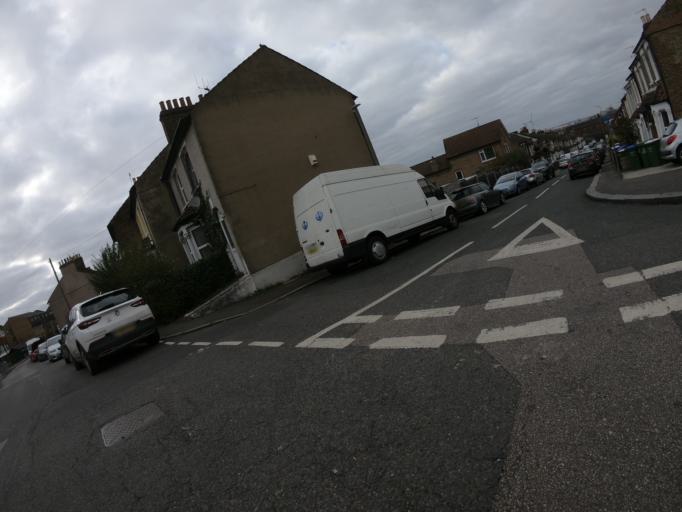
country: GB
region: England
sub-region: Greater London
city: Belvedere
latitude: 51.4889
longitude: 0.1455
